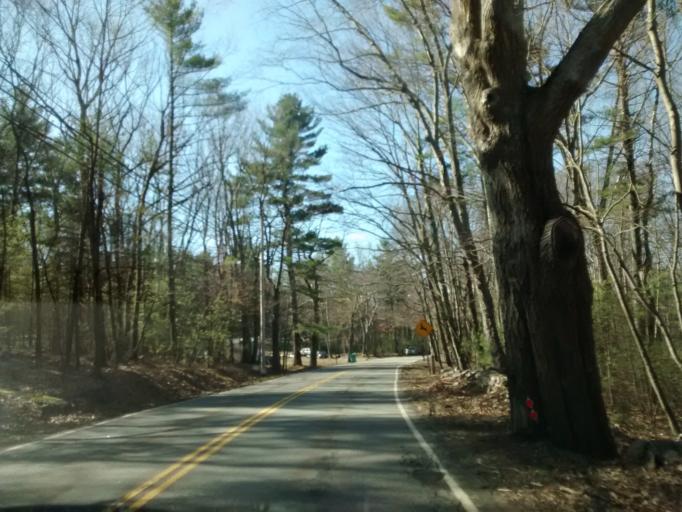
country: US
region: Massachusetts
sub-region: Worcester County
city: Upton
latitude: 42.2027
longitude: -71.6109
